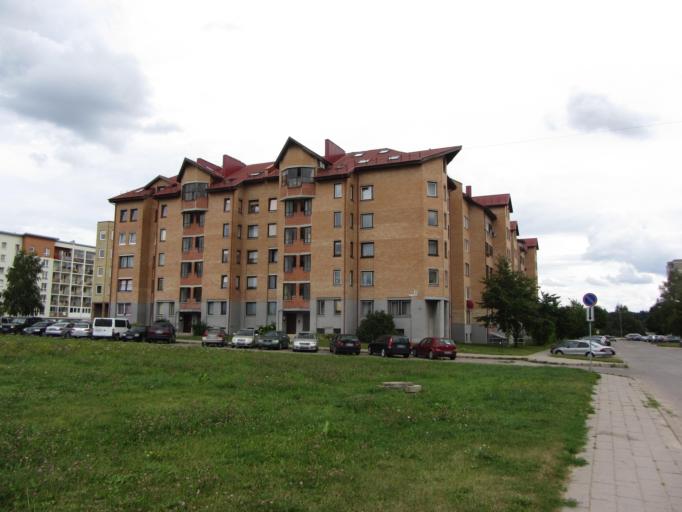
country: LT
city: Grigiskes
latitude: 54.6689
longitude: 25.0985
